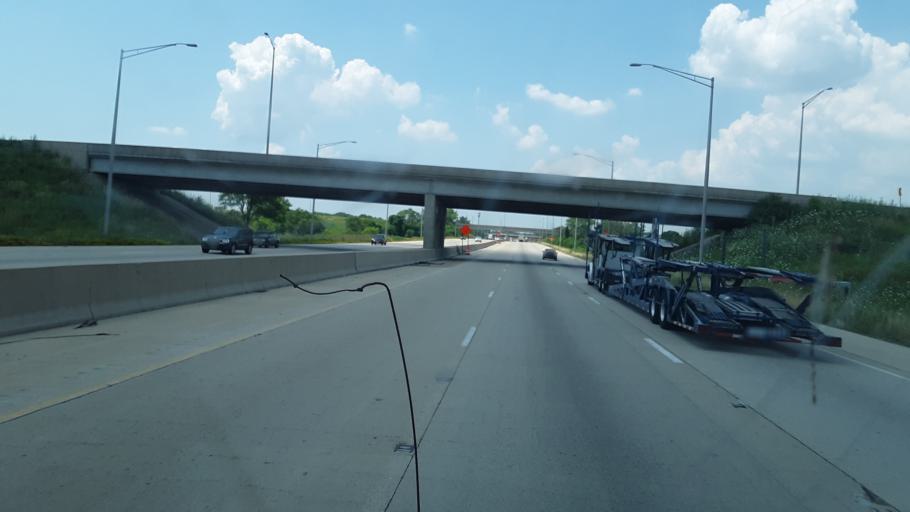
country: US
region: Illinois
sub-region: Will County
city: New Lenox
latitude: 41.5395
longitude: -87.9559
